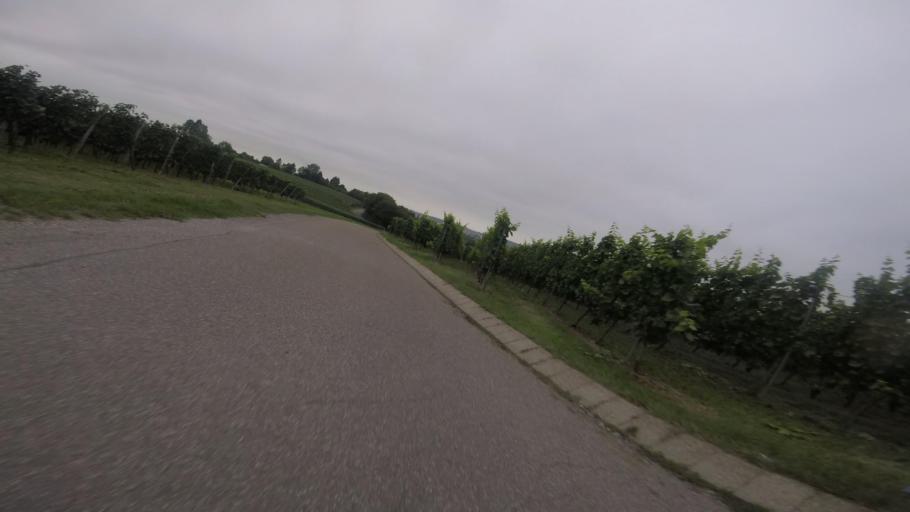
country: DE
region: Baden-Wuerttemberg
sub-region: Regierungsbezirk Stuttgart
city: Abstatt
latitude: 49.0603
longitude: 9.2974
